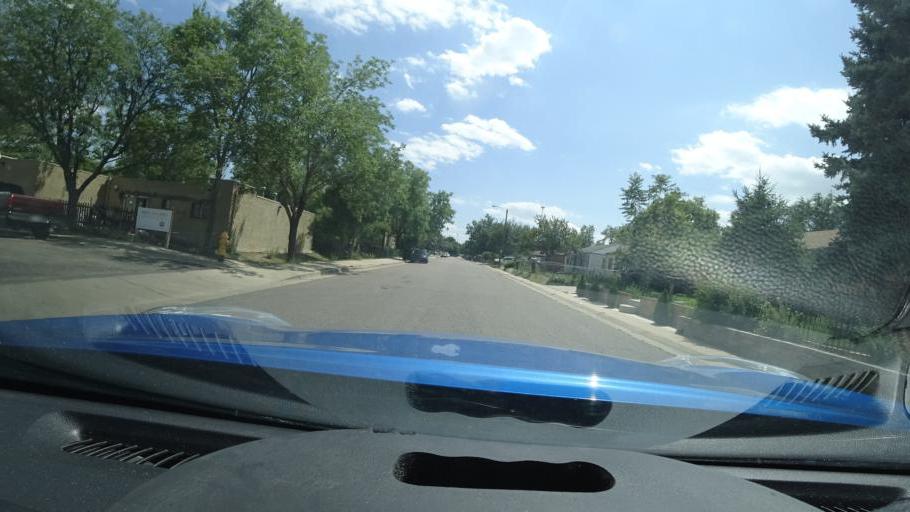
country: US
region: Colorado
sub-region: Jefferson County
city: Lakewood
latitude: 39.7039
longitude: -105.0461
